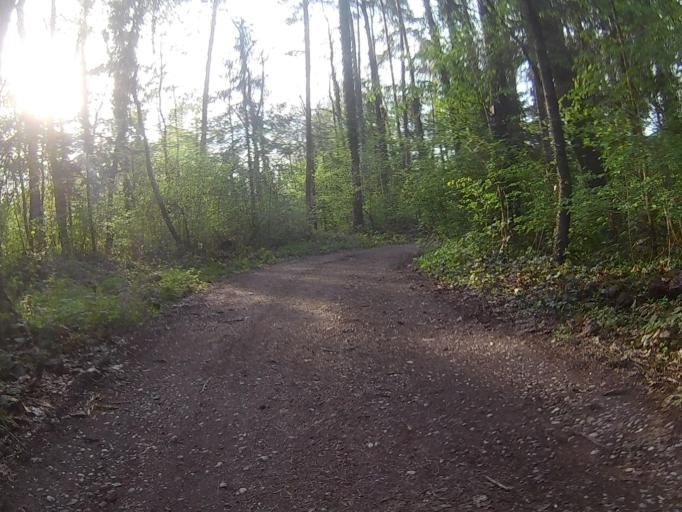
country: SI
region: Maribor
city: Limbus
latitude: 46.5634
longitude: 15.5924
